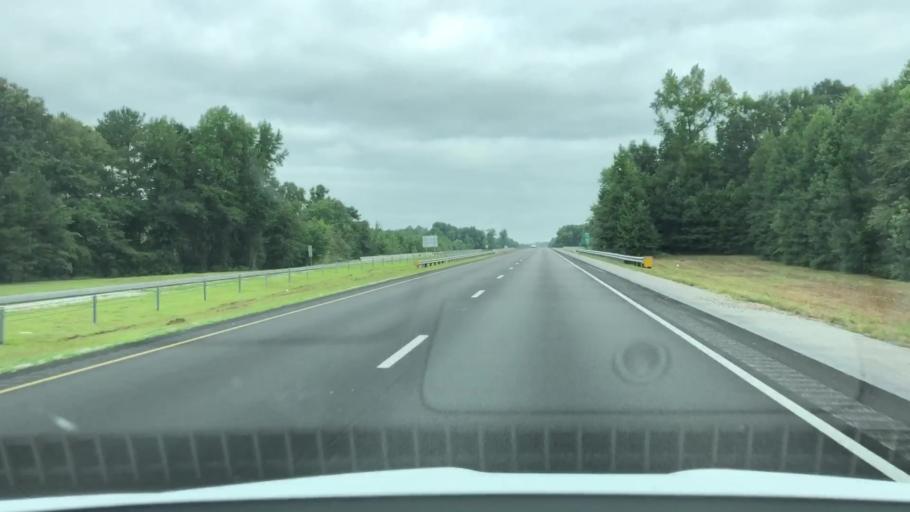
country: US
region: North Carolina
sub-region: Wayne County
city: Fremont
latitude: 35.5600
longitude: -77.9874
